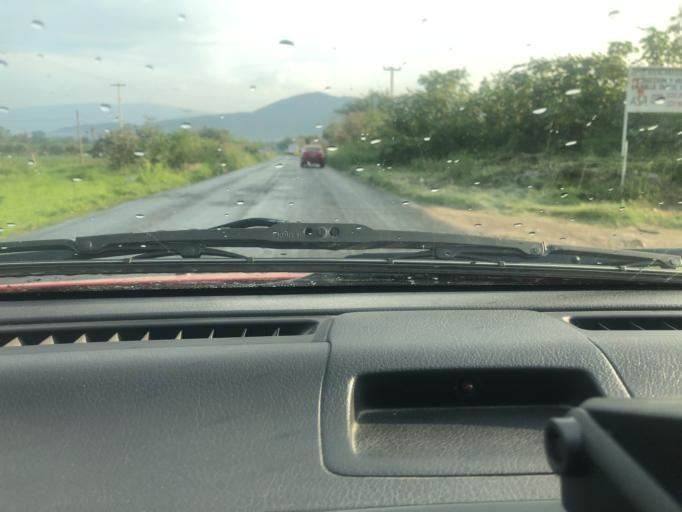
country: MX
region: Jalisco
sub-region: San Pedro Tlaquepaque
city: Santa Anita
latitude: 20.5506
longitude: -103.4199
